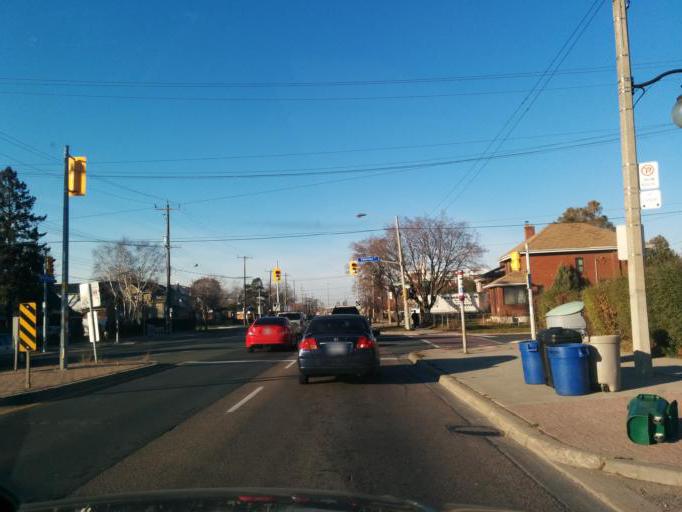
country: CA
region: Ontario
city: Etobicoke
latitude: 43.6058
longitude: -79.5469
